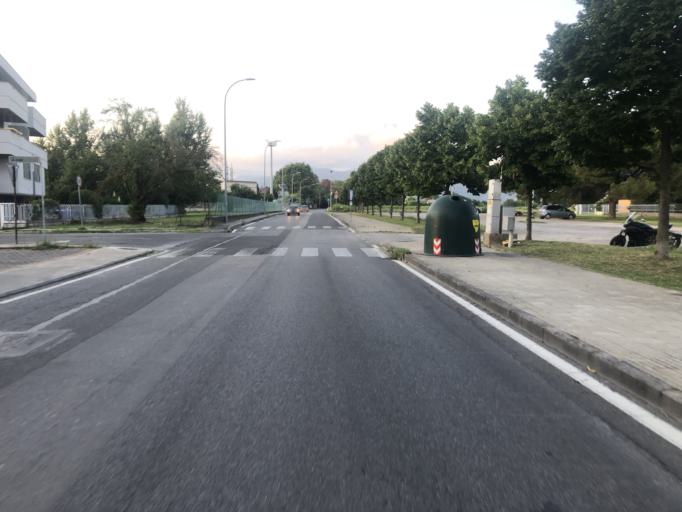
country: IT
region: Tuscany
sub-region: Province of Pisa
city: Pisa
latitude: 43.7330
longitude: 10.4083
